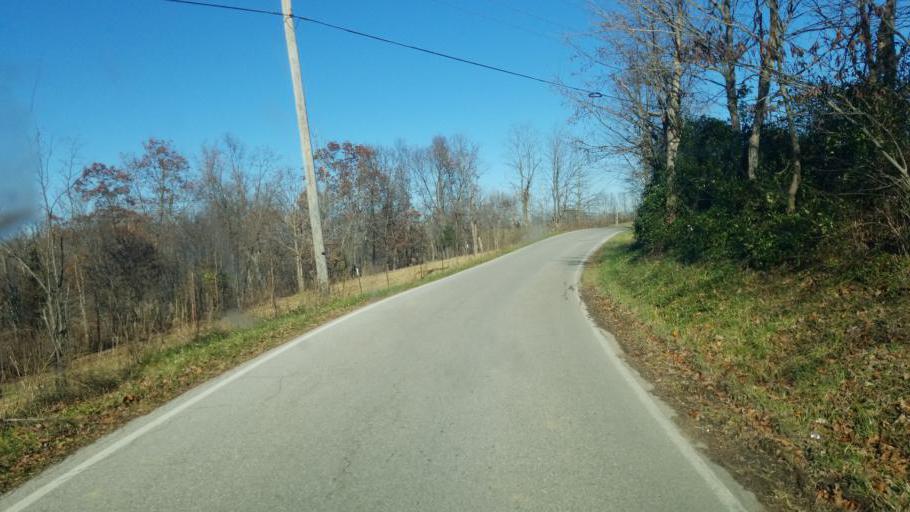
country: US
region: Kentucky
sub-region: Fleming County
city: Flemingsburg
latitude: 38.4614
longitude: -83.5228
